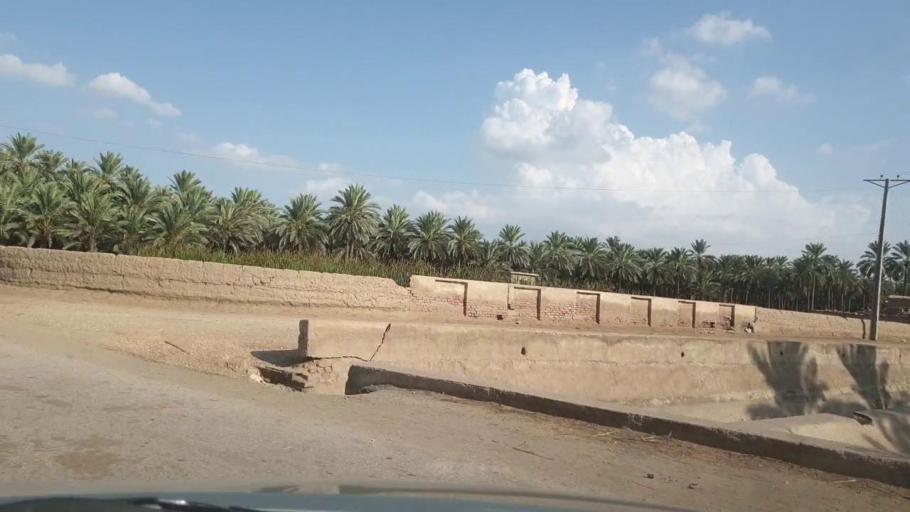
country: PK
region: Sindh
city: Sukkur
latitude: 27.6560
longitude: 68.8312
